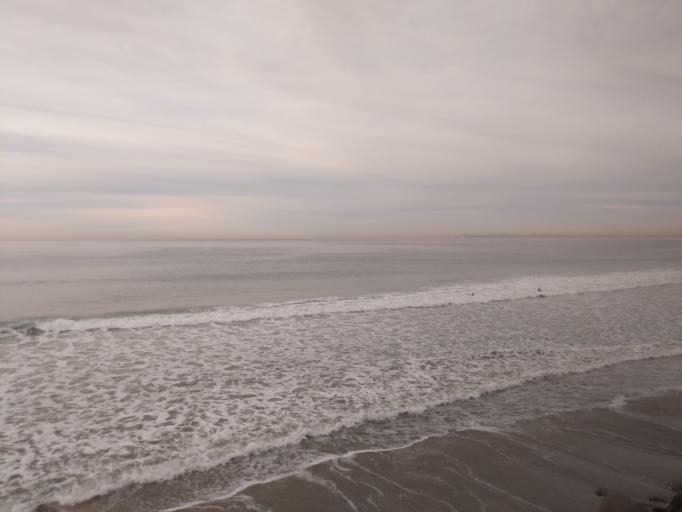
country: US
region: California
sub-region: Orange County
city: San Clemente
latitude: 33.4237
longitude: -117.6242
